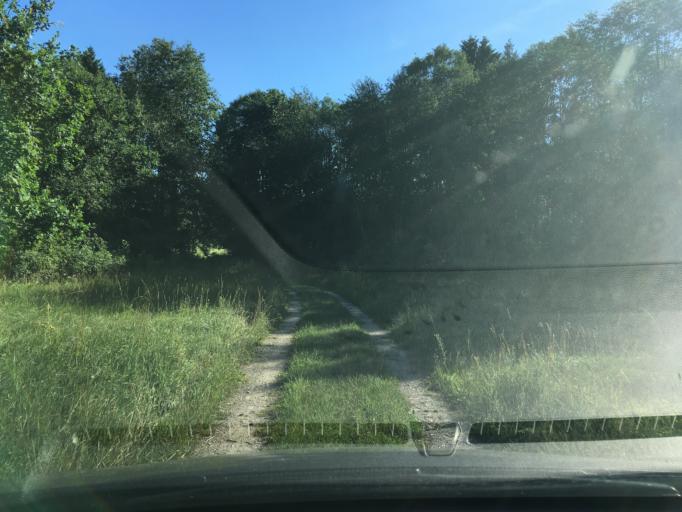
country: EE
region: Laeaene
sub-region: Lihula vald
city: Lihula
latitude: 58.5883
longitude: 23.7372
